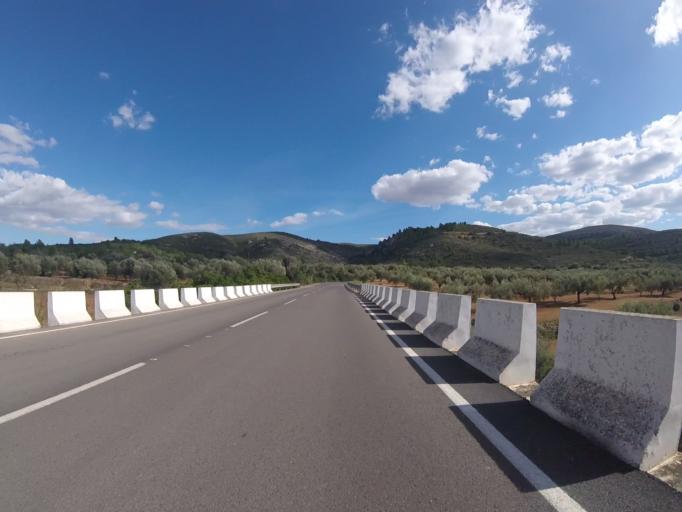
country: ES
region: Valencia
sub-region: Provincia de Castello
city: Cuevas de Vinroma
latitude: 40.3004
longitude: 0.1663
